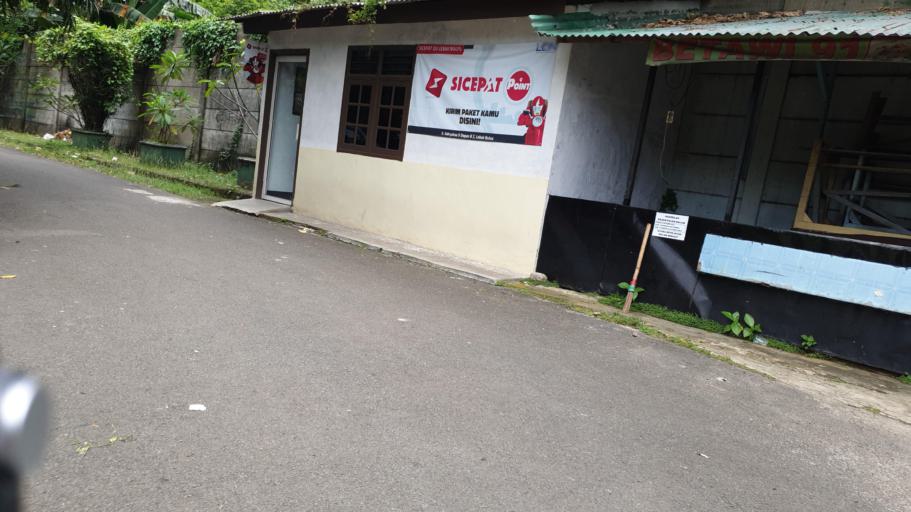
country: ID
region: Banten
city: South Tangerang
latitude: -6.2922
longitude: 106.7810
